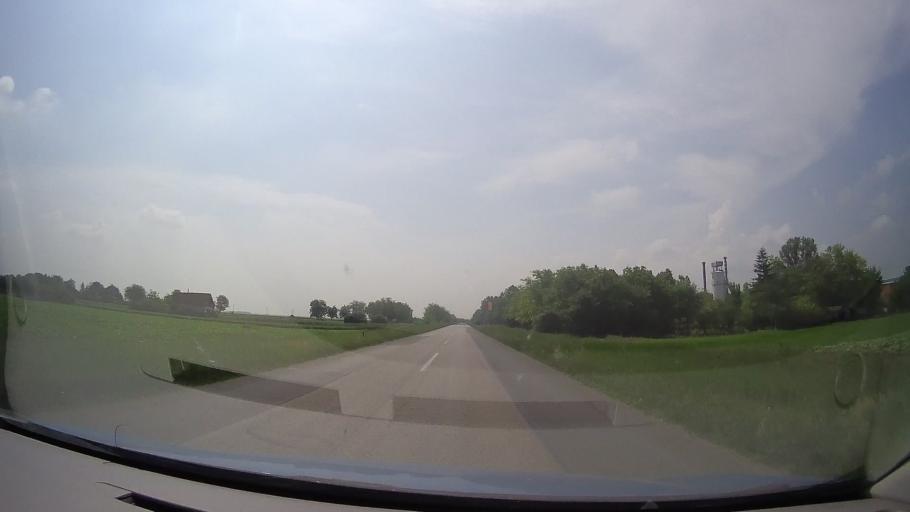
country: RS
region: Autonomna Pokrajina Vojvodina
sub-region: Juznobanatski Okrug
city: Kovacica
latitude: 45.0895
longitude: 20.6346
